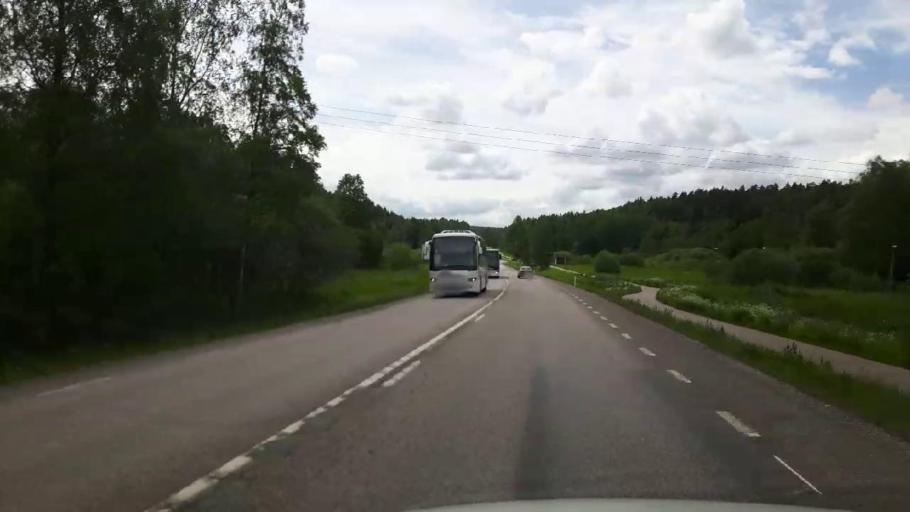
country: SE
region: Vaestmanland
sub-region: Fagersta Kommun
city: Fagersta
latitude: 59.9737
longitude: 15.7831
